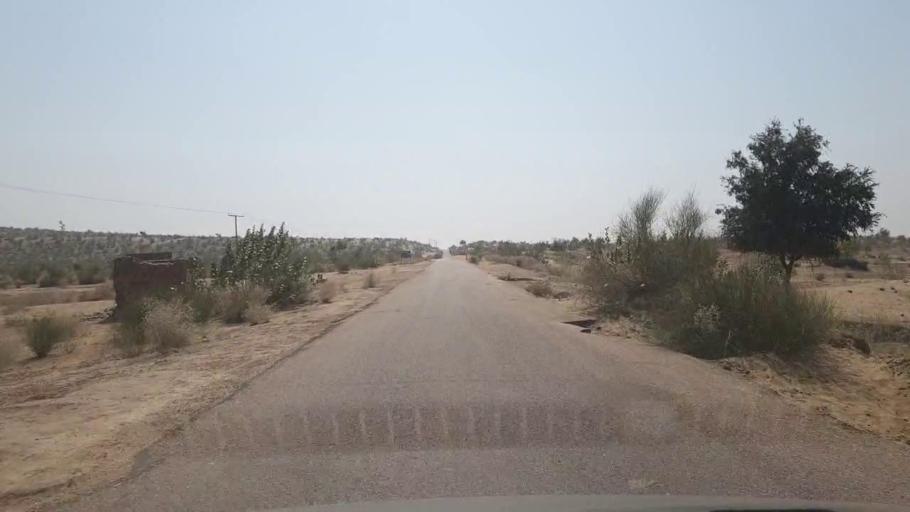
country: PK
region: Sindh
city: Chor
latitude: 25.6365
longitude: 70.1729
